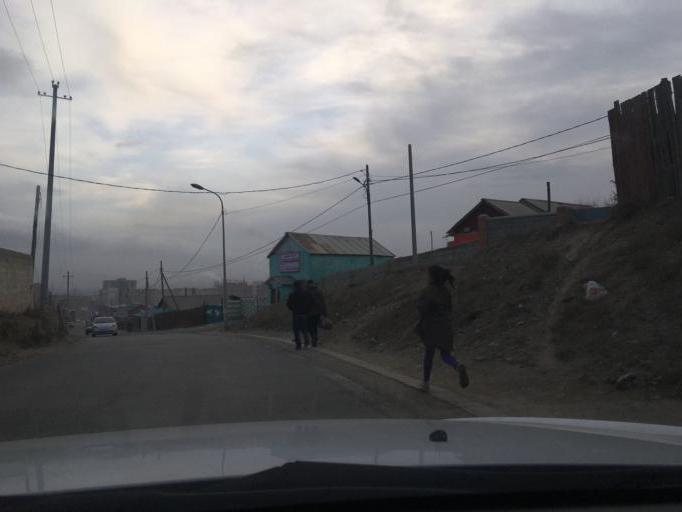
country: MN
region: Ulaanbaatar
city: Ulaanbaatar
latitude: 47.9205
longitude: 106.8346
